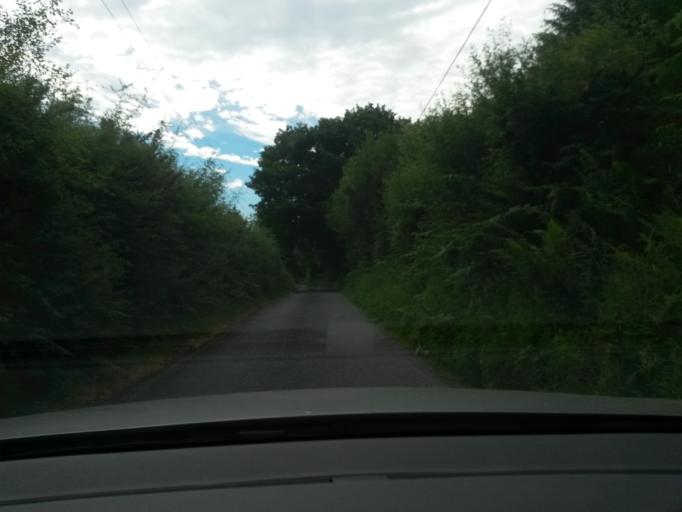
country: IE
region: Leinster
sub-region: Wicklow
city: Enniskerry
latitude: 53.1684
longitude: -6.2332
